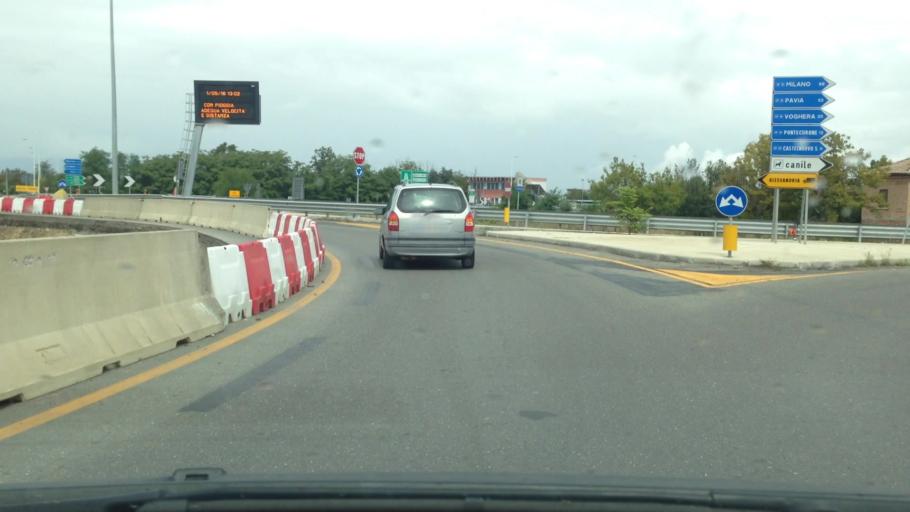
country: IT
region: Piedmont
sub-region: Provincia di Alessandria
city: Tortona
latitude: 44.9074
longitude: 8.8373
